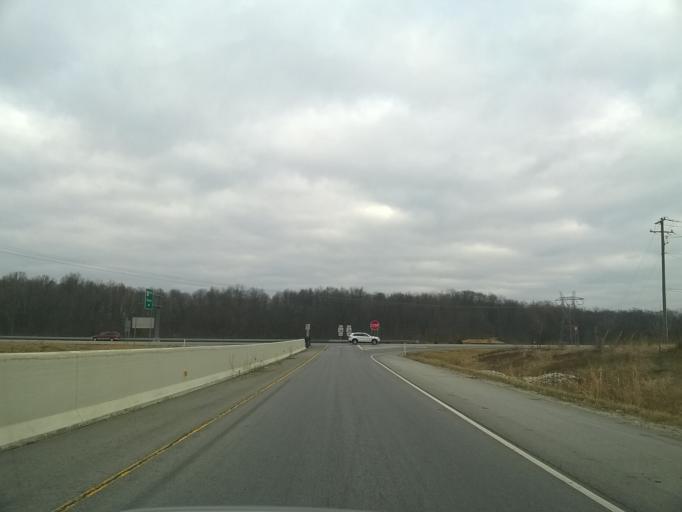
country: US
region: Indiana
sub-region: Hamilton County
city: Westfield
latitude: 40.0926
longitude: -86.1252
